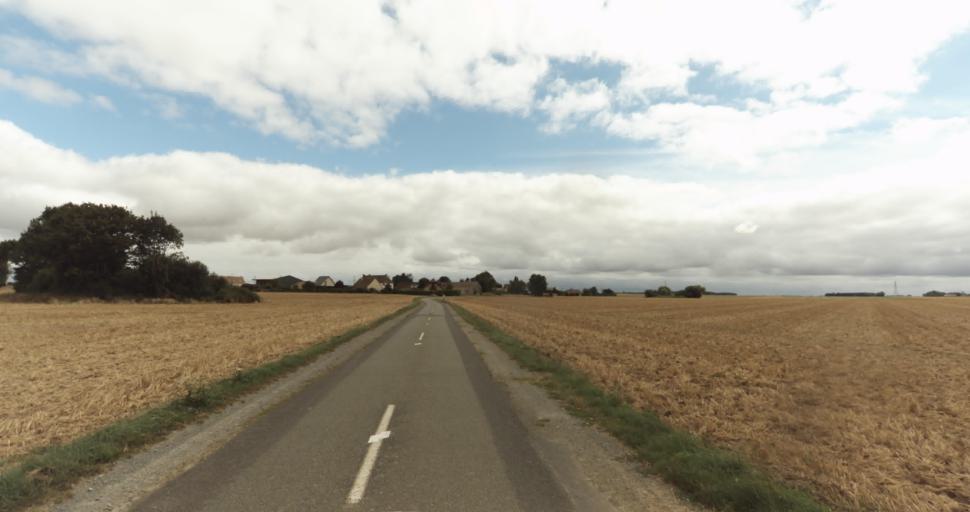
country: FR
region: Haute-Normandie
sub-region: Departement de l'Eure
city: Evreux
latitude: 48.9354
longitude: 1.2172
